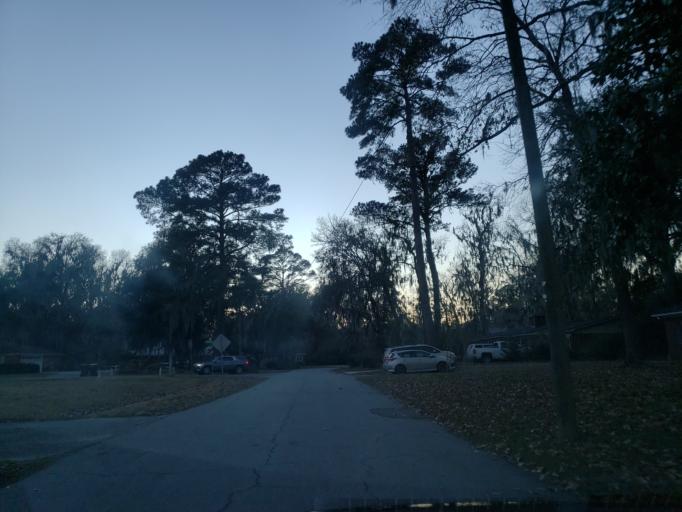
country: US
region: Georgia
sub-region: Chatham County
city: Thunderbolt
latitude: 32.0193
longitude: -81.0854
